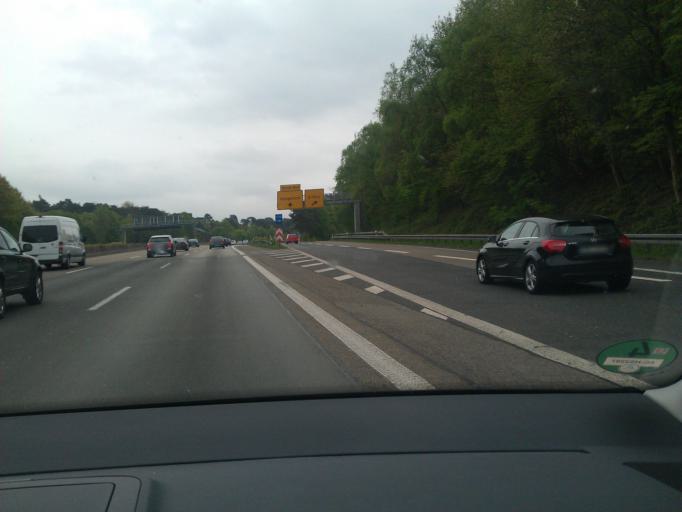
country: DE
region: North Rhine-Westphalia
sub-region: Regierungsbezirk Koln
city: Rath
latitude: 50.9161
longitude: 7.1011
